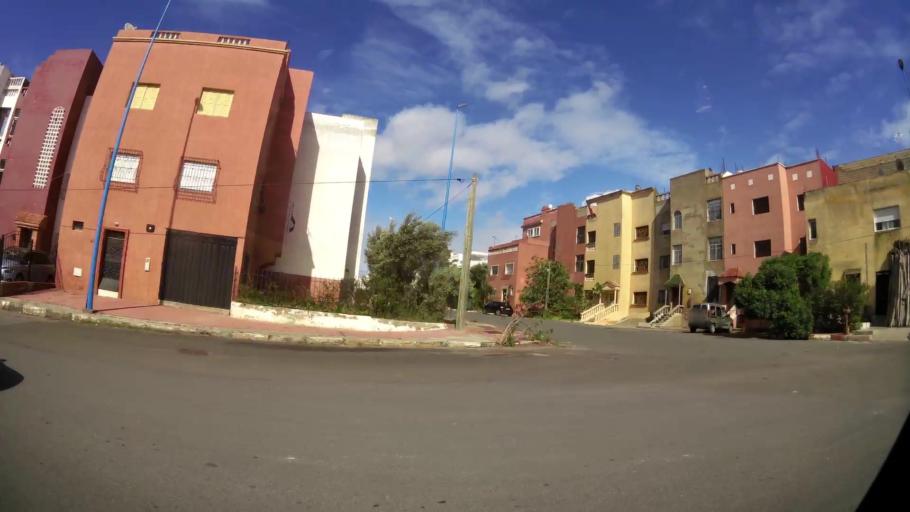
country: MA
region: Grand Casablanca
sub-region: Casablanca
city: Casablanca
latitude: 33.5685
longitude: -7.6964
